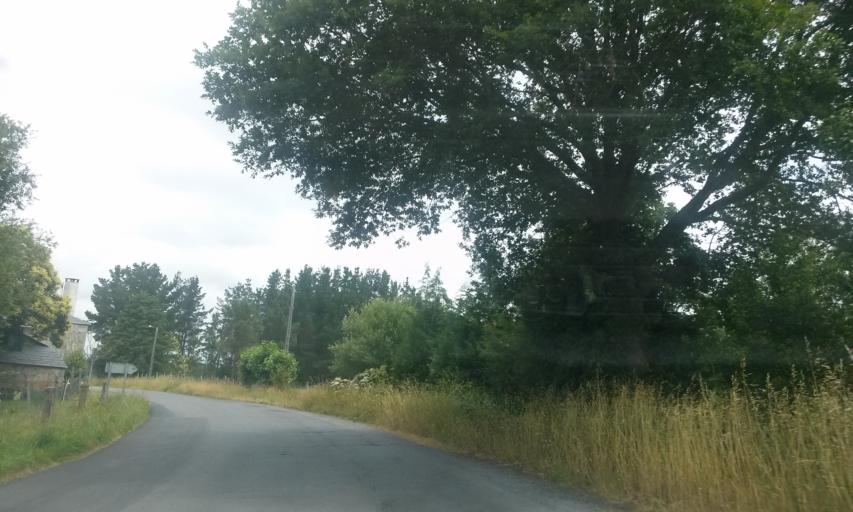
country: ES
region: Galicia
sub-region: Provincia de Lugo
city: Friol
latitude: 43.0872
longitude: -7.8100
